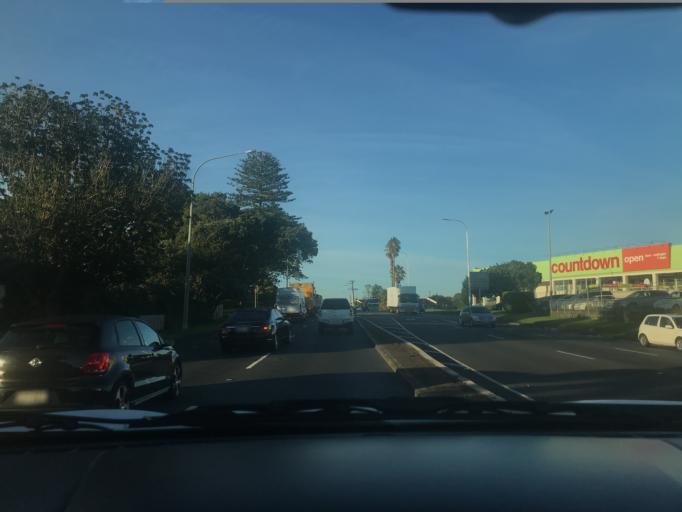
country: NZ
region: Auckland
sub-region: Auckland
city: Tamaki
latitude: -36.9090
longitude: 174.8385
